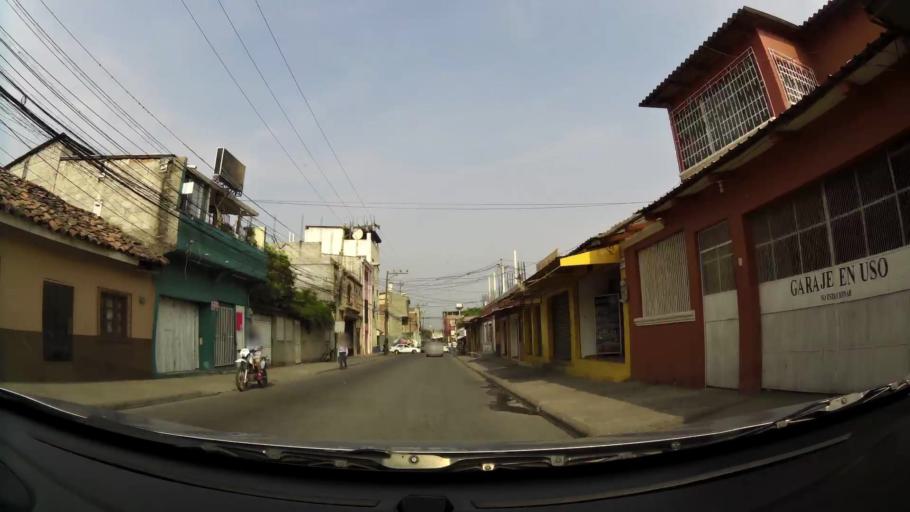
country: HN
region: Comayagua
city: Comayagua
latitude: 14.4562
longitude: -87.6400
